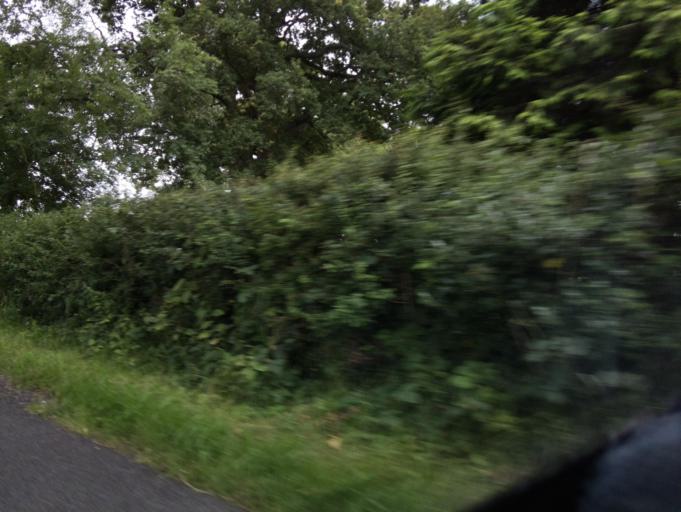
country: GB
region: England
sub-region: Solihull
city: Dickens Heath
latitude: 52.3780
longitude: -1.8401
